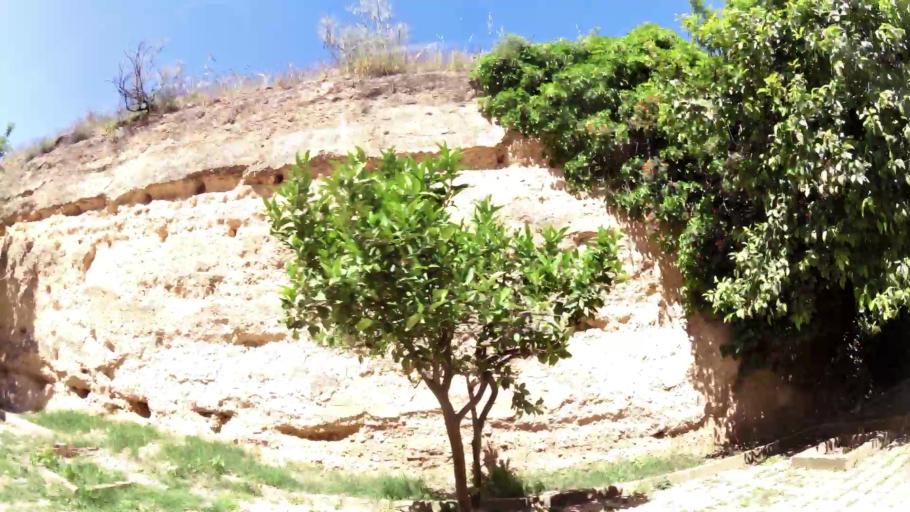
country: MA
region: Meknes-Tafilalet
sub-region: Meknes
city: Meknes
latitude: 33.8802
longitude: -5.5602
